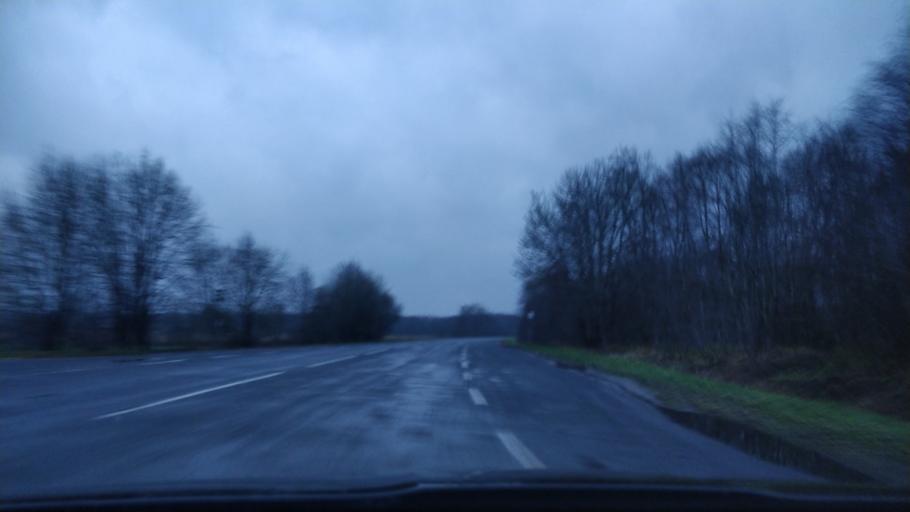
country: EE
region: Laeaene
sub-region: Lihula vald
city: Lihula
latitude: 58.7064
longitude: 23.8625
